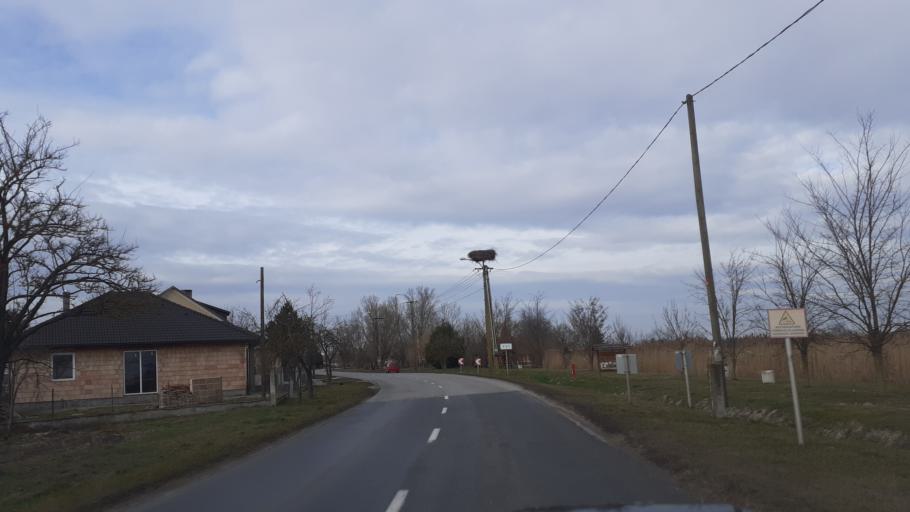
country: HU
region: Fejer
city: Szabadbattyan
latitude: 47.0756
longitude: 18.4143
